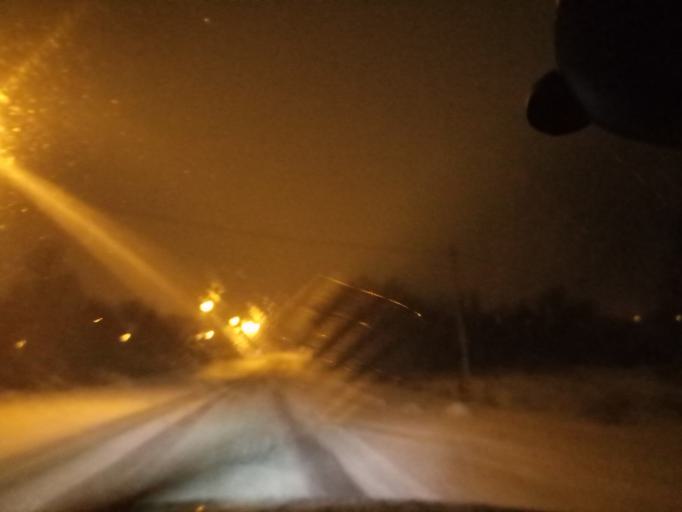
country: RU
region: Tula
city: Novomoskovsk
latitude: 53.9976
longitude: 38.2954
